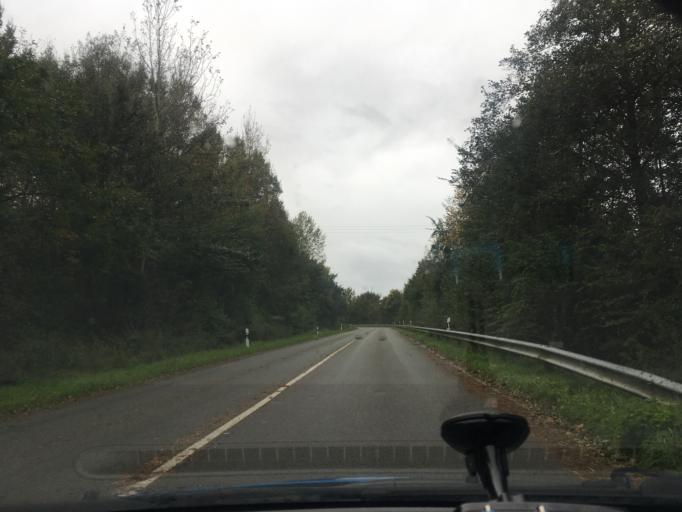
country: DE
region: Lower Saxony
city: Handorf
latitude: 53.3867
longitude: 10.3447
